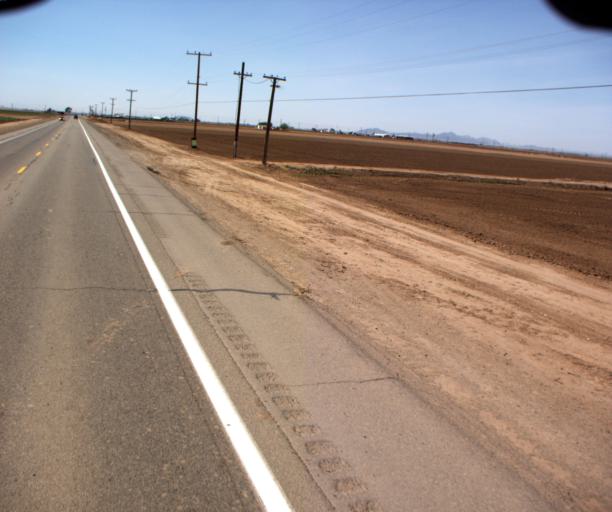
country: US
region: Arizona
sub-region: Yuma County
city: Fortuna Foothills
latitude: 32.6997
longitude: -114.4543
